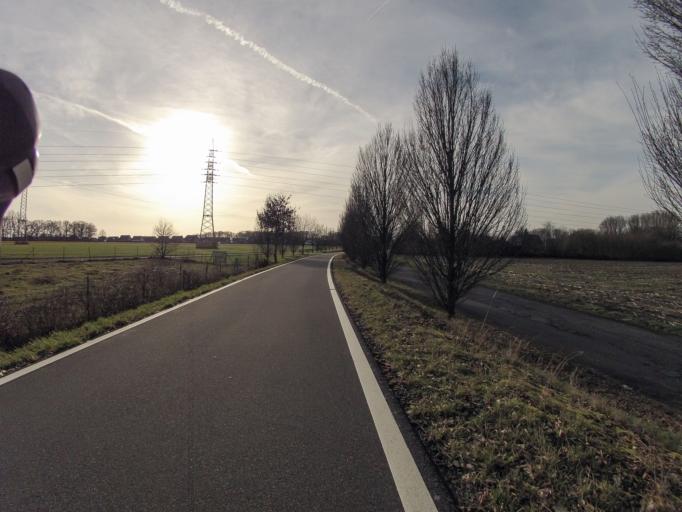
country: DE
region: North Rhine-Westphalia
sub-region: Regierungsbezirk Munster
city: Rheine
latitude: 52.2445
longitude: 7.4560
